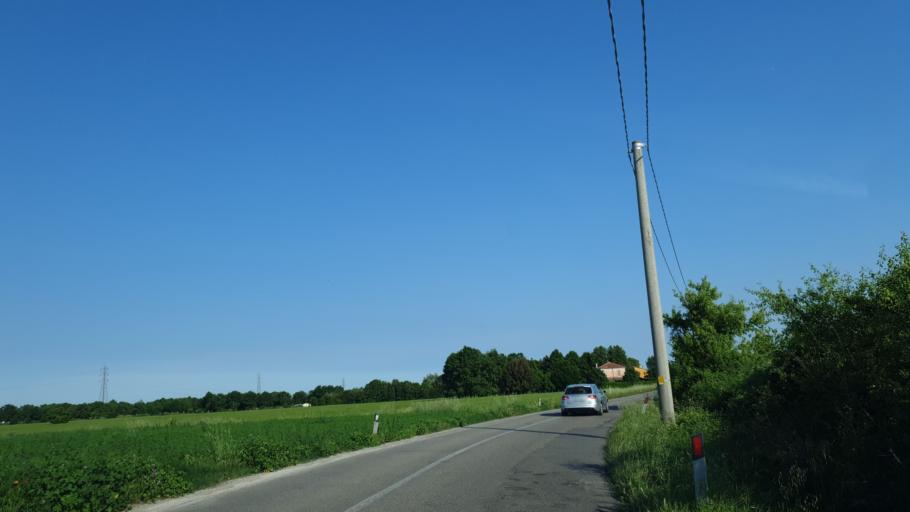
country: IT
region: Emilia-Romagna
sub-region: Provincia di Ravenna
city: Ravenna
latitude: 44.4141
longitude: 12.2243
